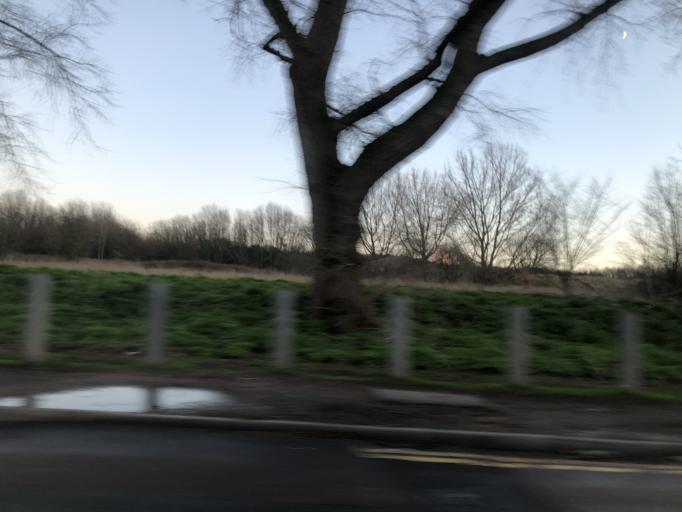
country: GB
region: England
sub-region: Greater London
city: Woolwich
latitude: 51.4748
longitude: 0.0482
